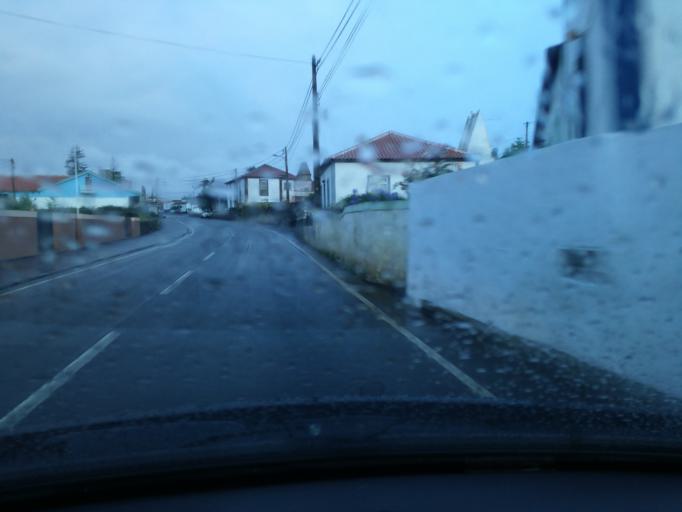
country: PT
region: Azores
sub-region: Praia da Vitoria
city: Praia da Vitoria
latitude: 38.7092
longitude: -27.0606
